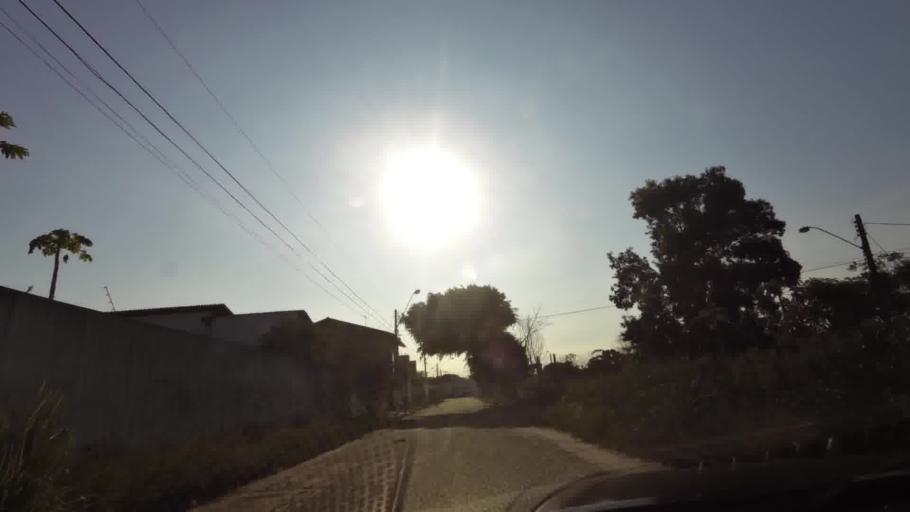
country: BR
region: Espirito Santo
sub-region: Vila Velha
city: Vila Velha
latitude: -20.4762
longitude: -40.3492
